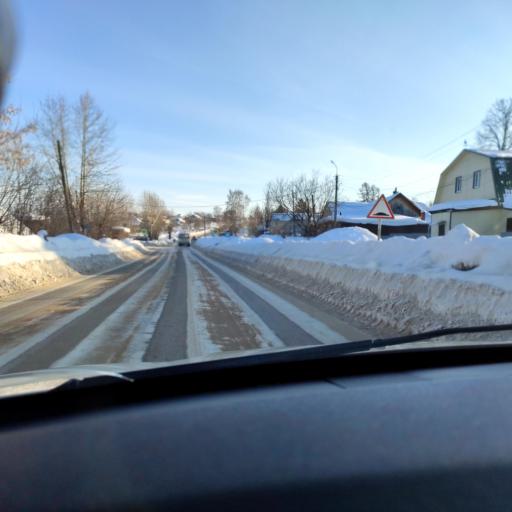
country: RU
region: Perm
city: Polazna
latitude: 58.2967
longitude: 56.4159
